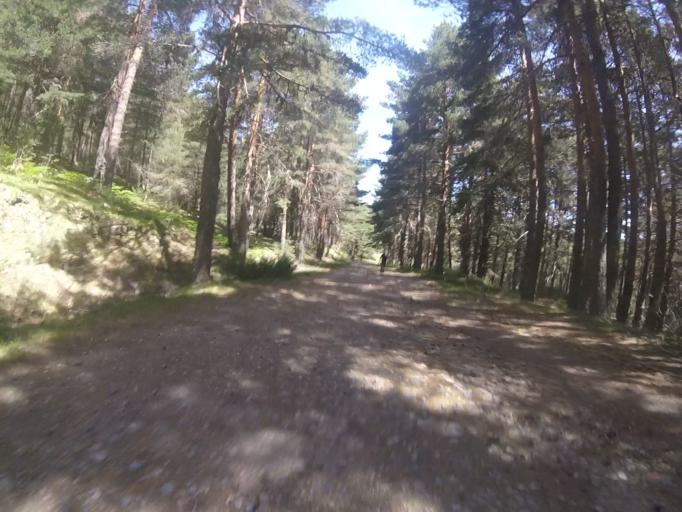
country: ES
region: Madrid
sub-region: Provincia de Madrid
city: Cercedilla
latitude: 40.8113
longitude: -4.0565
